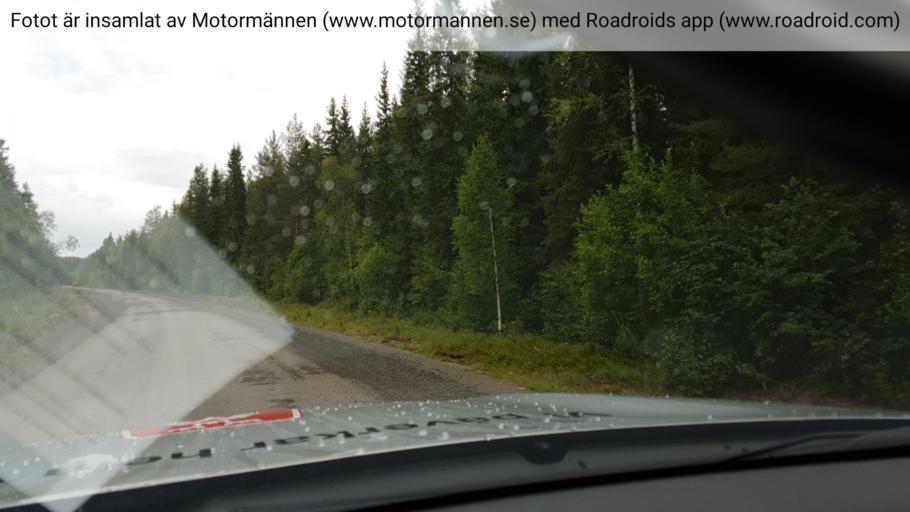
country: SE
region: Norrbotten
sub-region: Alvsbyns Kommun
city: AElvsbyn
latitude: 65.9325
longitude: 21.2471
